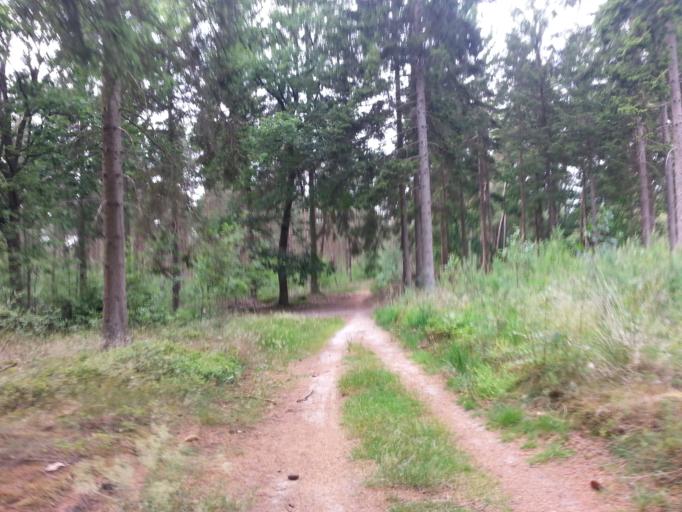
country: NL
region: Utrecht
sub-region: Gemeente Amersfoort
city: Randenbroek
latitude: 52.1142
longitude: 5.3836
